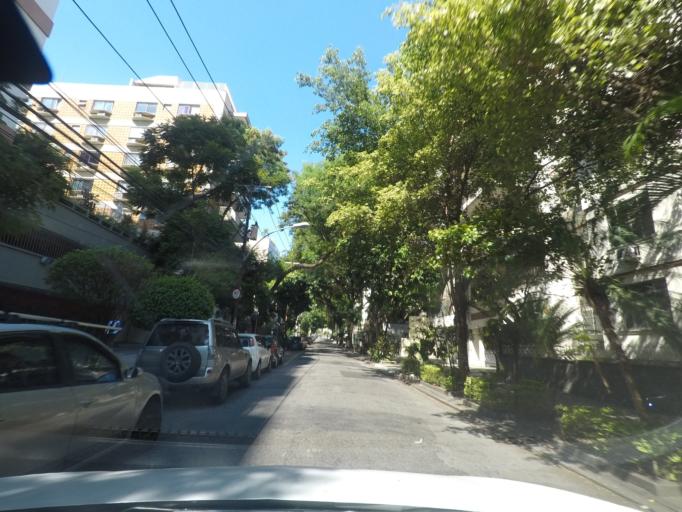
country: BR
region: Rio de Janeiro
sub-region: Rio De Janeiro
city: Rio de Janeiro
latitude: -22.9330
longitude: -43.2388
